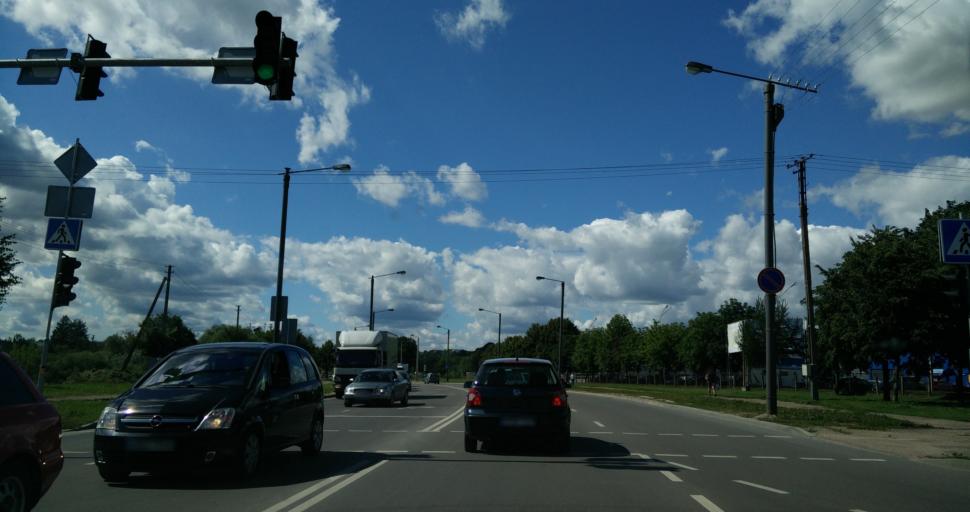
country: LT
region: Kauno apskritis
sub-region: Kauno rajonas
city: Akademija (Kaunas)
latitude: 54.9201
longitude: 23.8269
